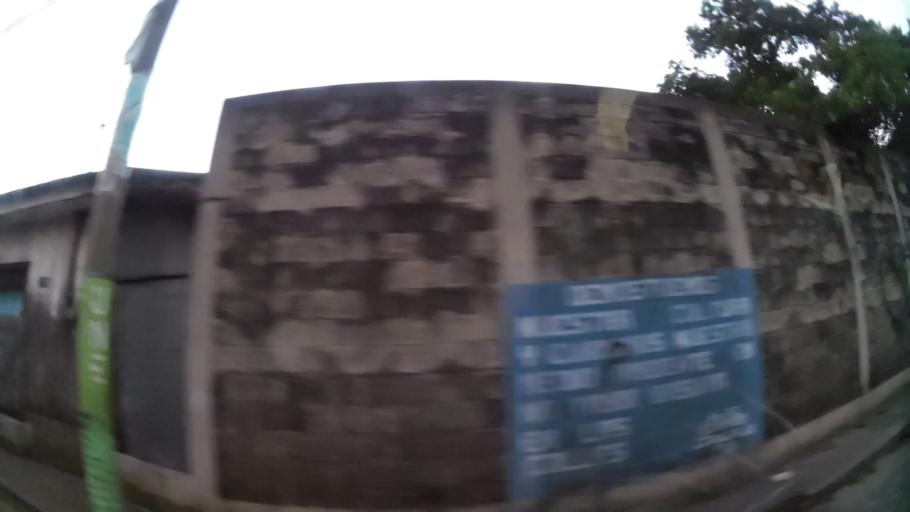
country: GT
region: Retalhuleu
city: San Felipe
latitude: 14.6232
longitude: -91.5951
